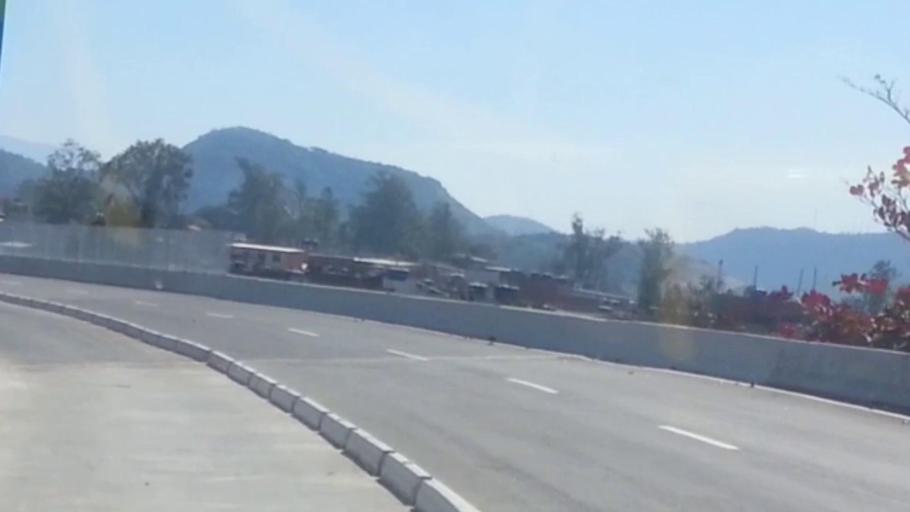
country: BR
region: Rio de Janeiro
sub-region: Nilopolis
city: Nilopolis
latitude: -22.9489
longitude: -43.3903
